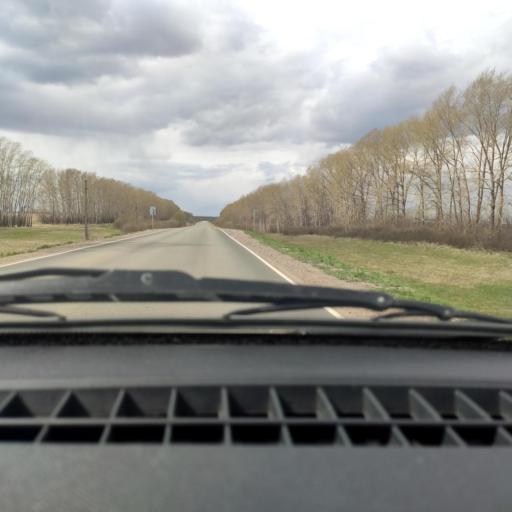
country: RU
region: Bashkortostan
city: Alekseyevka
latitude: 55.0581
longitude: 55.1126
